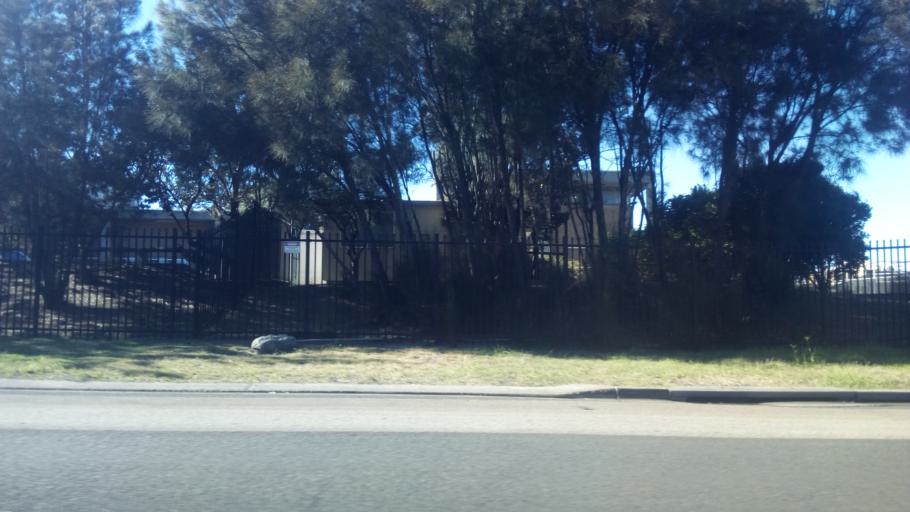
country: AU
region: New South Wales
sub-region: Wollongong
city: Coniston
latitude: -34.4417
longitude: 150.8965
